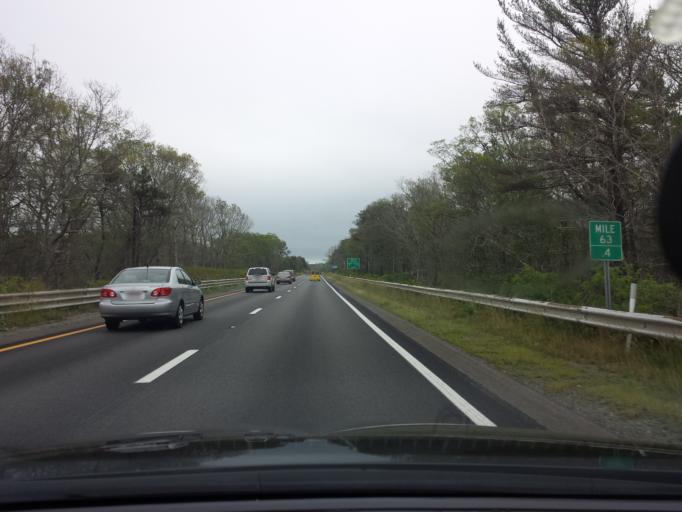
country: US
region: Massachusetts
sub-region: Barnstable County
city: West Barnstable
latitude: 41.7137
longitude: -70.4159
